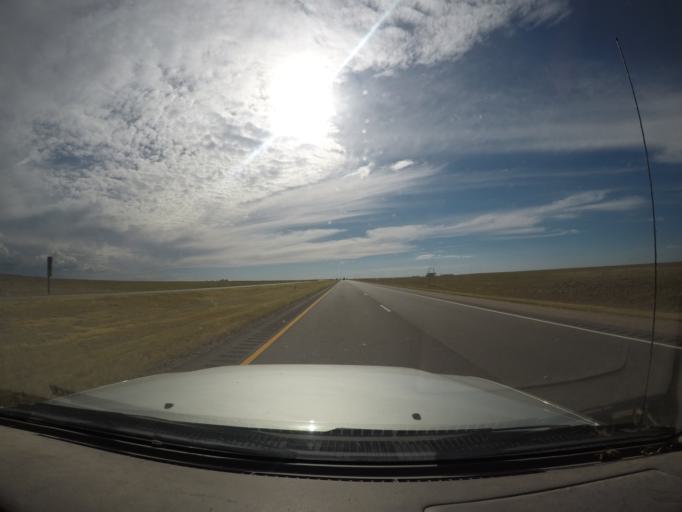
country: US
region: Wyoming
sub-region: Laramie County
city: Pine Bluffs
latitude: 41.1915
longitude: -103.8748
